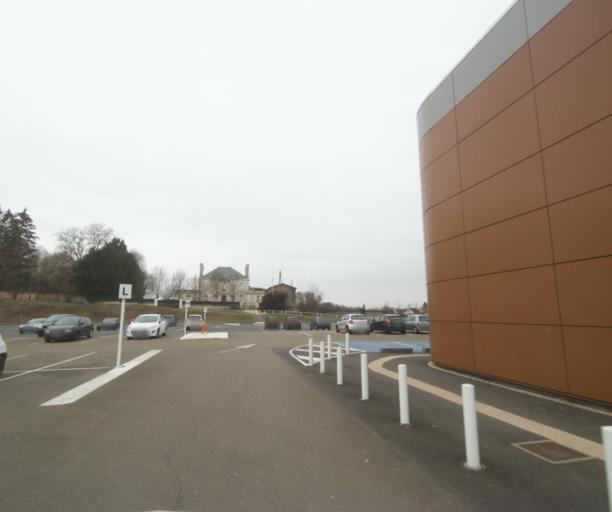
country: FR
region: Champagne-Ardenne
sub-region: Departement de la Haute-Marne
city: Saint-Dizier
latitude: 48.6279
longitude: 4.9701
